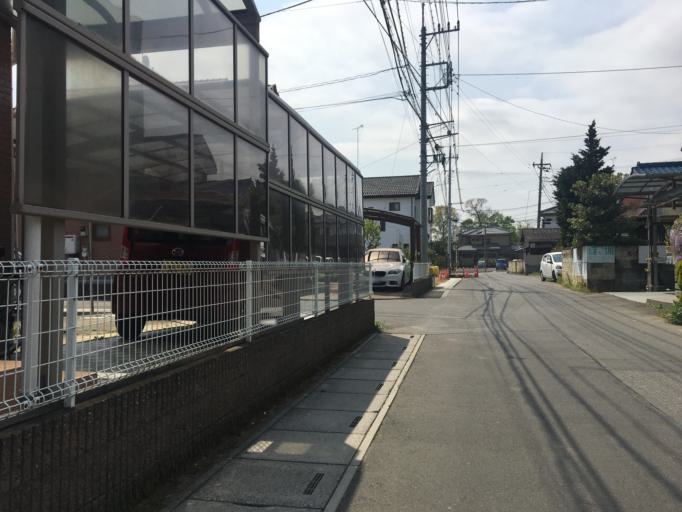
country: JP
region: Saitama
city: Kamifukuoka
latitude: 35.8898
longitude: 139.5267
